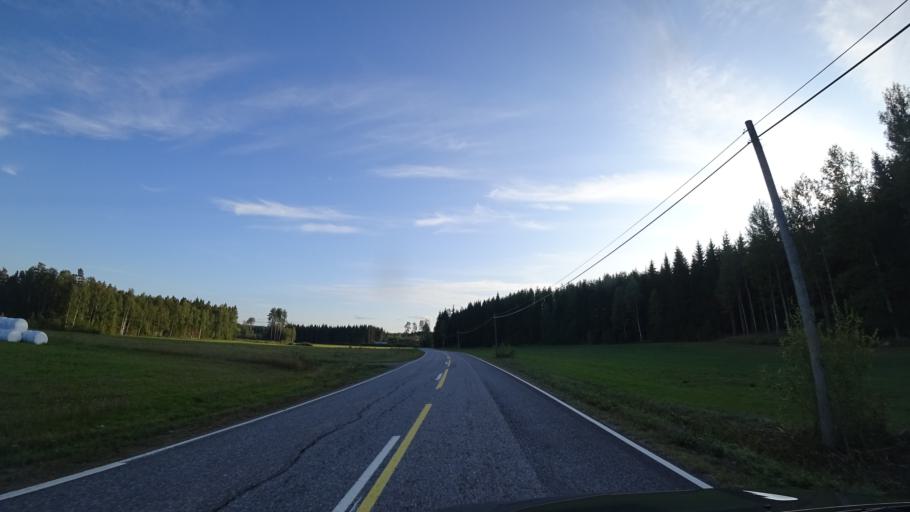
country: FI
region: Haeme
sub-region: Haemeenlinna
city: Tuulos
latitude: 61.0076
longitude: 24.8528
